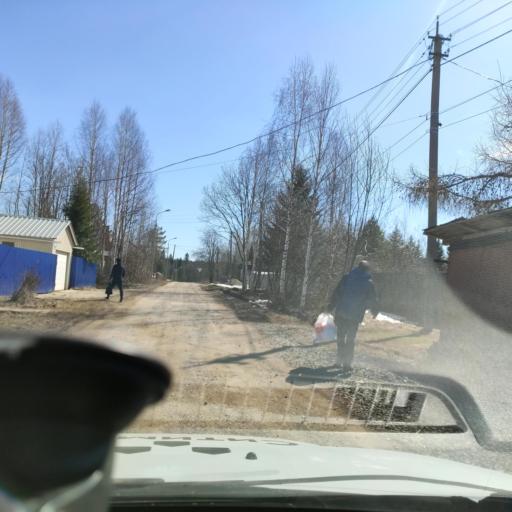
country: RU
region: Perm
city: Ferma
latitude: 57.9286
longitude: 56.4208
